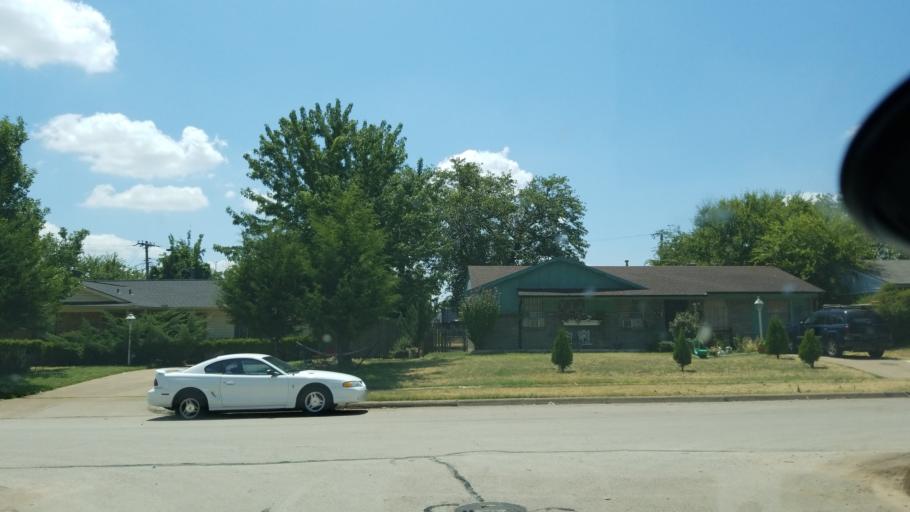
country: US
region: Texas
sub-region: Dallas County
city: Duncanville
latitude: 32.6645
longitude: -96.8921
